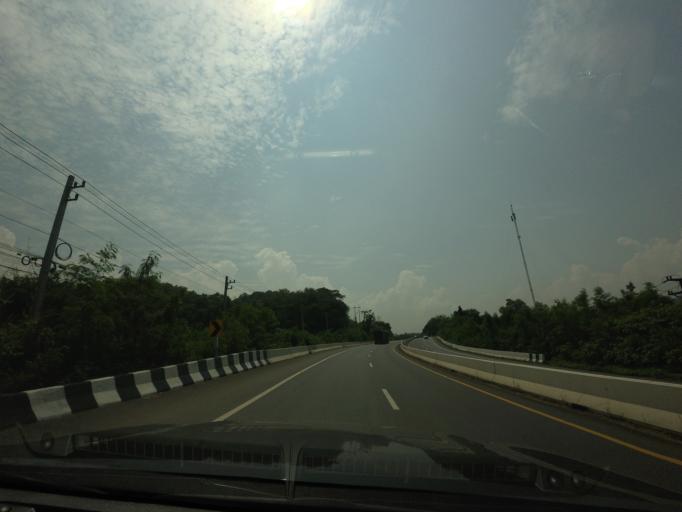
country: TH
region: Phrae
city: Den Chai
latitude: 17.9366
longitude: 100.0615
